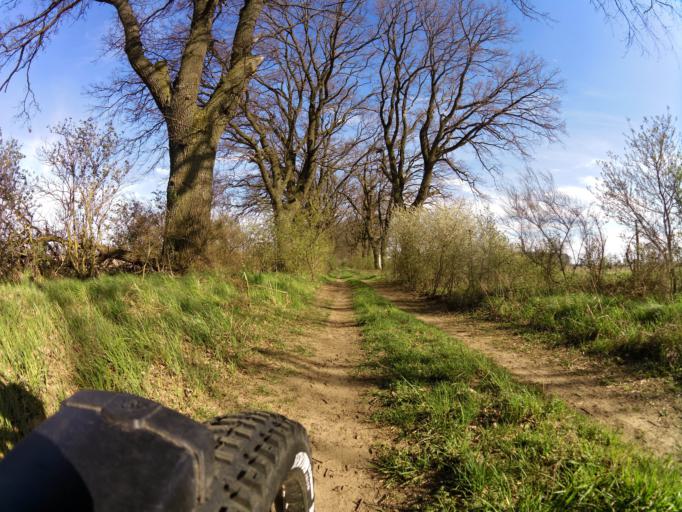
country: PL
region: West Pomeranian Voivodeship
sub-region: Powiat lobeski
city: Resko
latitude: 53.7802
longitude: 15.5536
